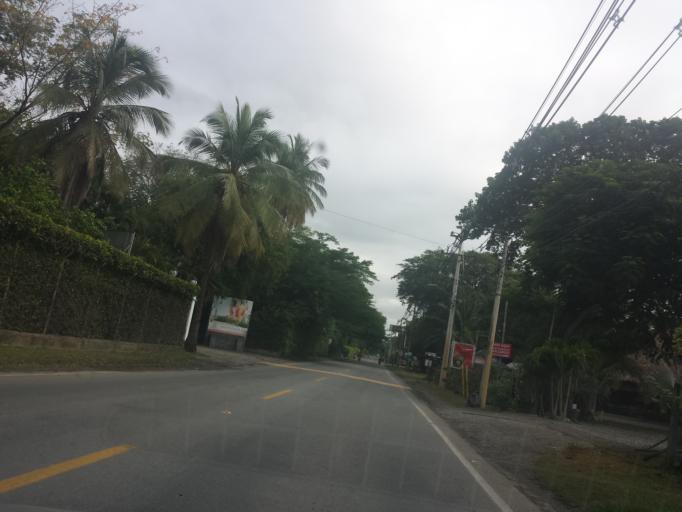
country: CO
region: Antioquia
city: Antioquia
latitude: 6.5348
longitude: -75.8189
